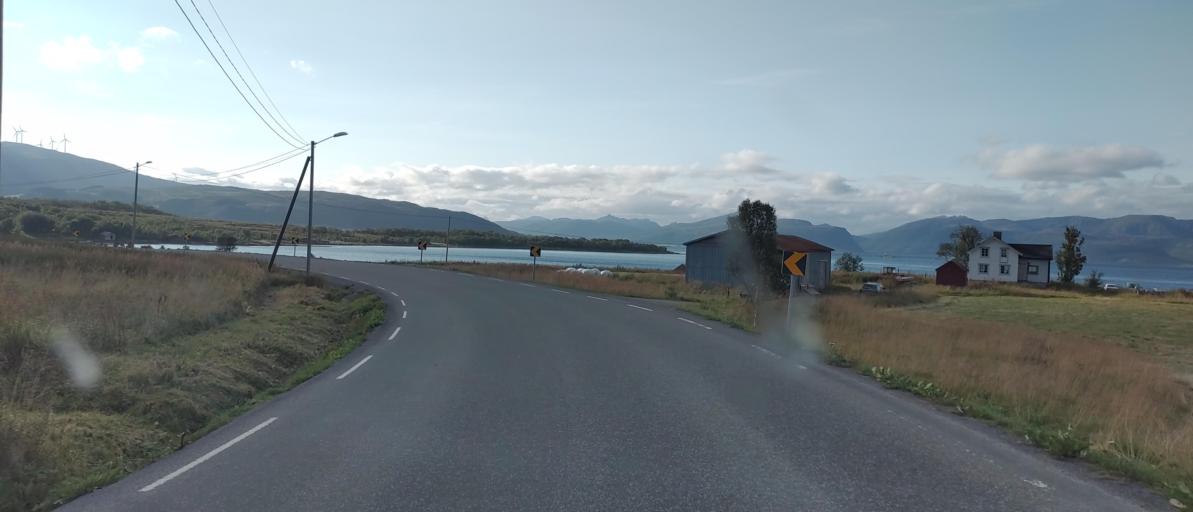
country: NO
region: Nordland
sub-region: Sortland
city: Sortland
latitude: 68.7250
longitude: 15.4788
